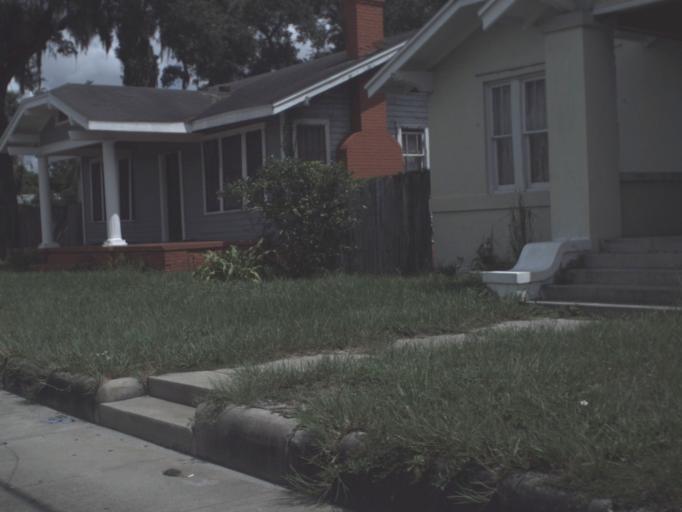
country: US
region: Florida
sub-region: Hillsborough County
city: Tampa
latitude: 27.9981
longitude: -82.4594
